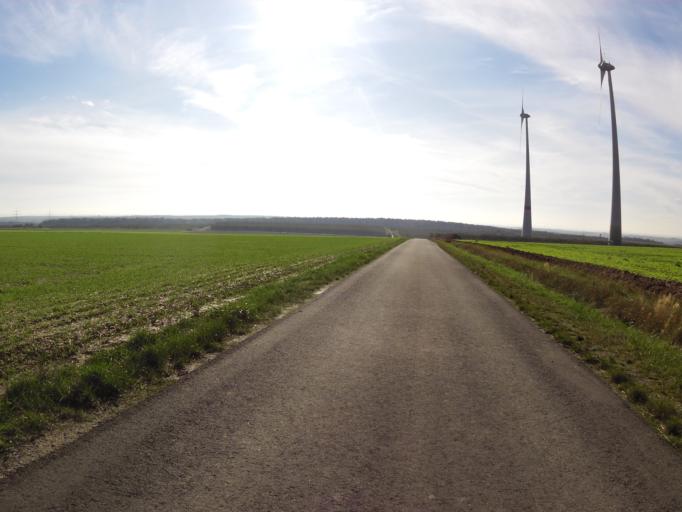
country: DE
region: Bavaria
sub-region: Regierungsbezirk Unterfranken
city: Sommerhausen
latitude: 49.7177
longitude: 10.0462
